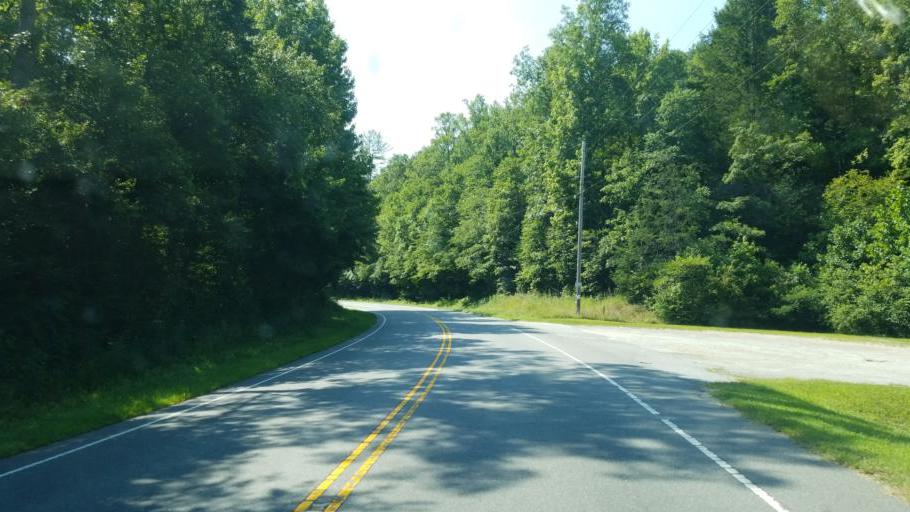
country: US
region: North Carolina
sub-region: Burke County
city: Glen Alpine
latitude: 35.8231
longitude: -81.7936
